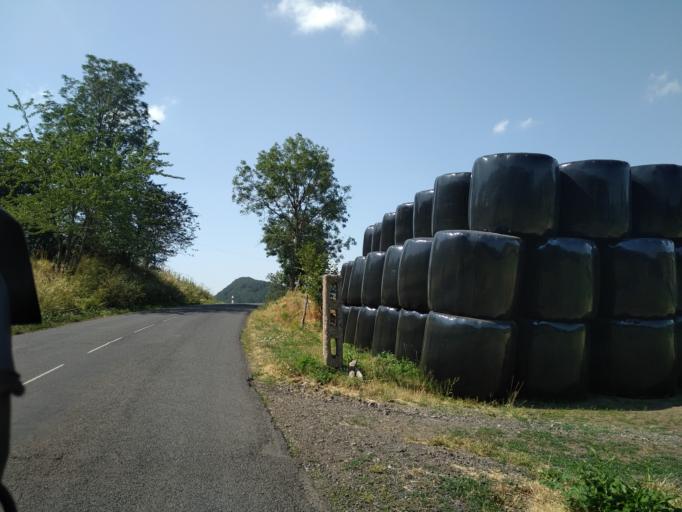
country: FR
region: Auvergne
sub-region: Departement du Cantal
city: Riom-es-Montagnes
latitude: 45.1953
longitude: 2.7166
